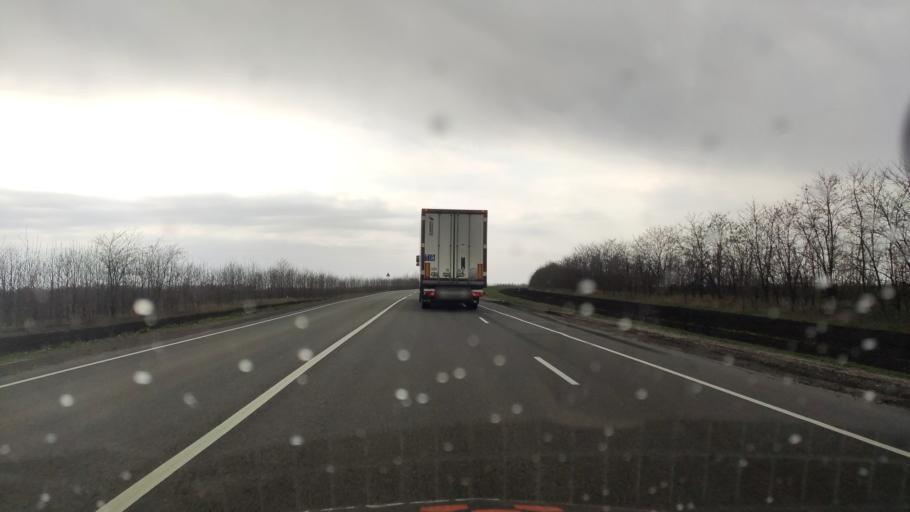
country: RU
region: Voronezj
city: Nizhnedevitsk
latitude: 51.5658
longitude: 38.3474
